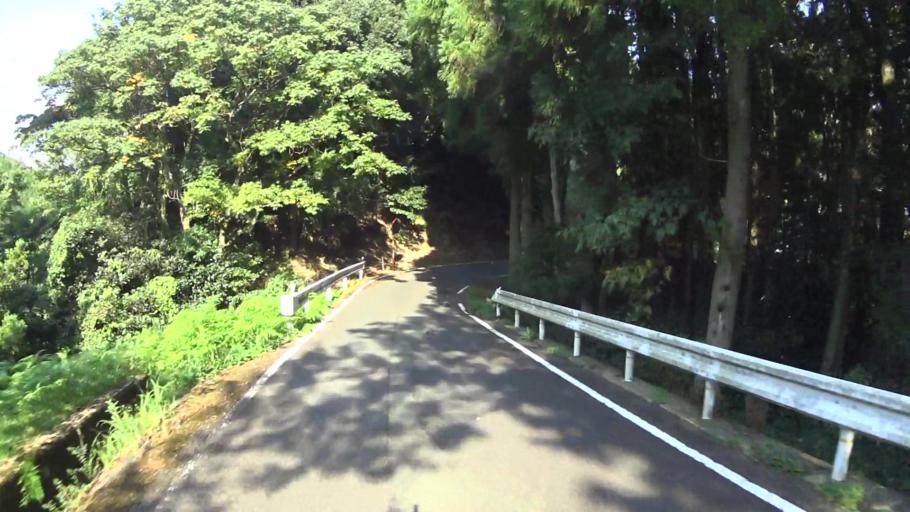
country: JP
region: Kyoto
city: Miyazu
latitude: 35.5667
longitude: 135.1378
